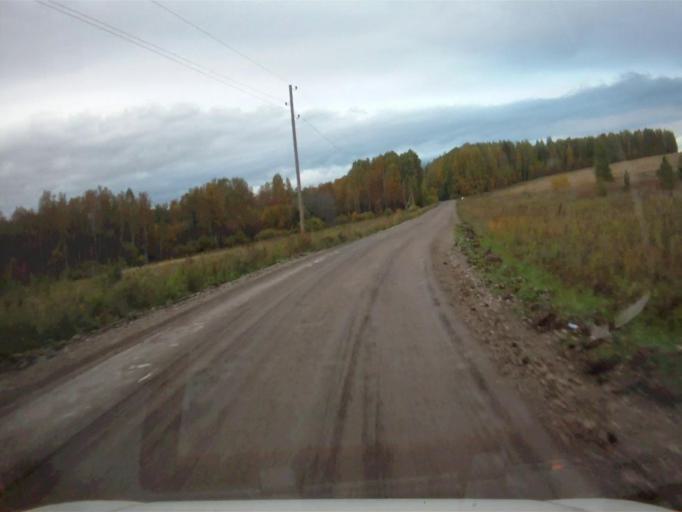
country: RU
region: Sverdlovsk
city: Mikhaylovsk
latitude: 56.1907
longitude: 59.1892
